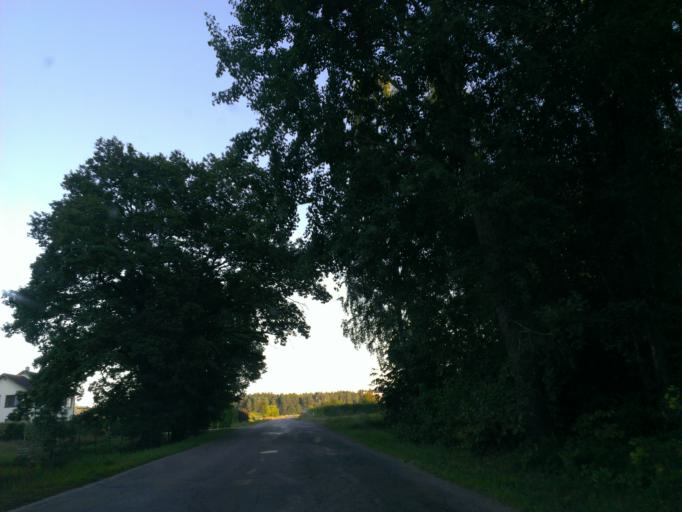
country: LV
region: Garkalne
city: Garkalne
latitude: 57.0663
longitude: 24.3746
